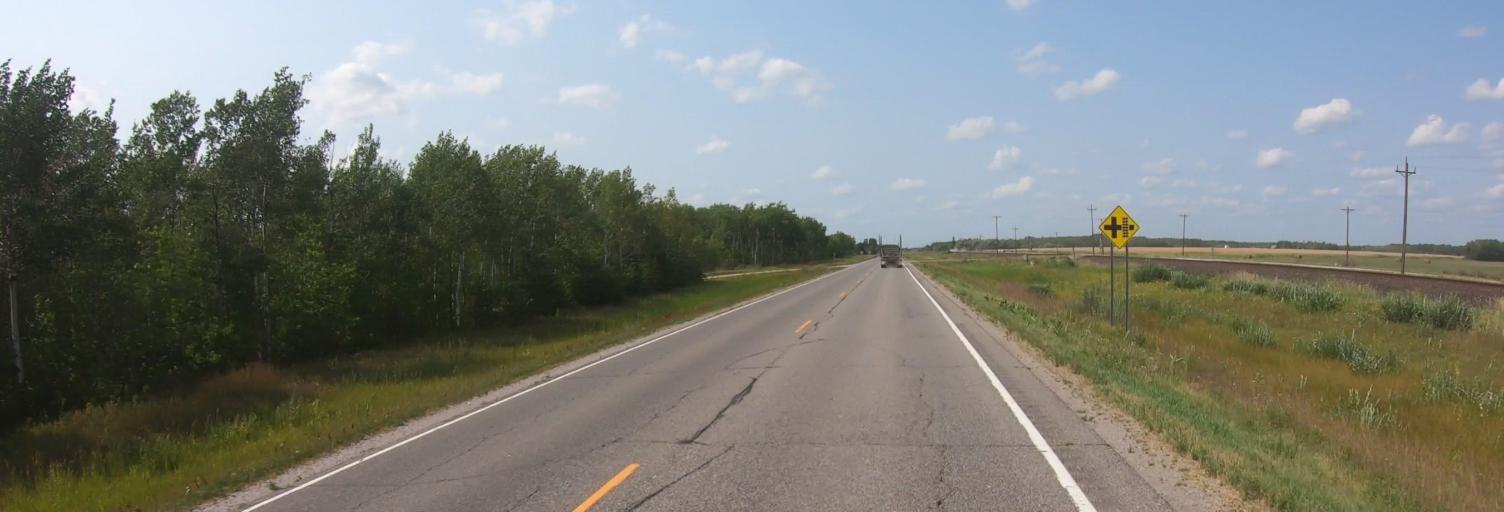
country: US
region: Minnesota
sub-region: Roseau County
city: Warroad
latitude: 48.8799
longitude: -95.2851
